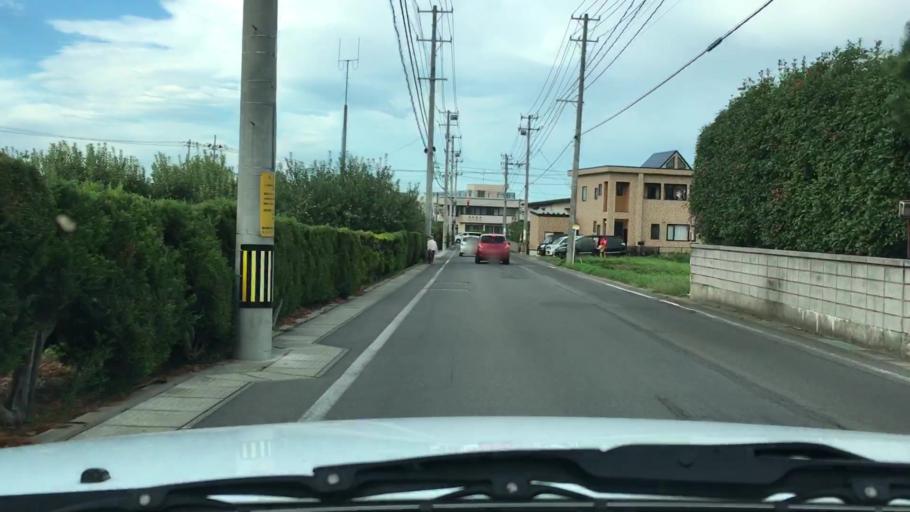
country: JP
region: Aomori
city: Hirosaki
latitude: 40.5856
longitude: 140.4613
